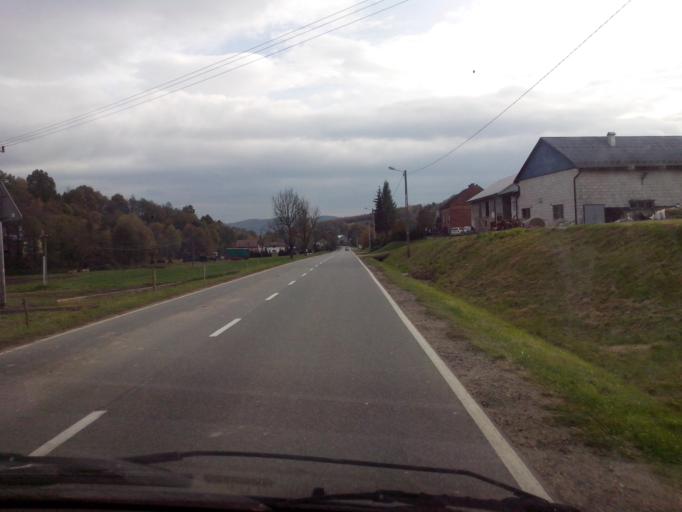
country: PL
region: Subcarpathian Voivodeship
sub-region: Powiat strzyzowski
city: Wisniowa
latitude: 49.8942
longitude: 21.6433
